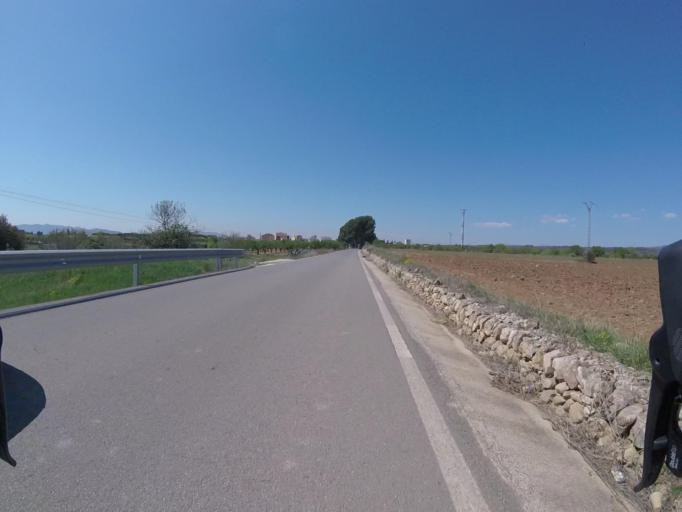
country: ES
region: Valencia
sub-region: Provincia de Castello
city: Benlloch
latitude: 40.2151
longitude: 0.0335
